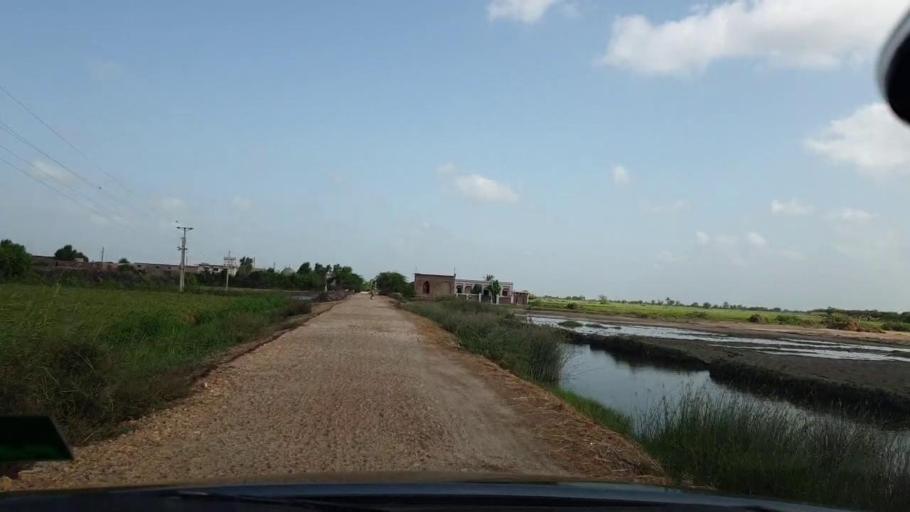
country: PK
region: Sindh
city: Tando Bago
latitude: 24.6430
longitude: 69.0937
